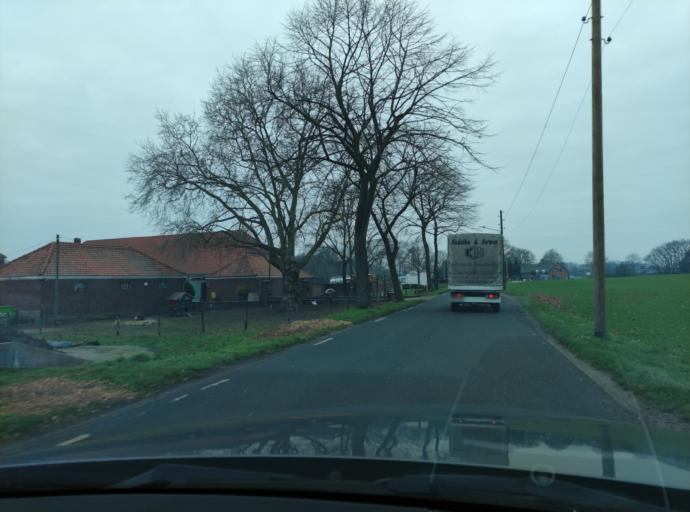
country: DE
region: North Rhine-Westphalia
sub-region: Regierungsbezirk Dusseldorf
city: Rheurdt
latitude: 51.4287
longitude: 6.4211
